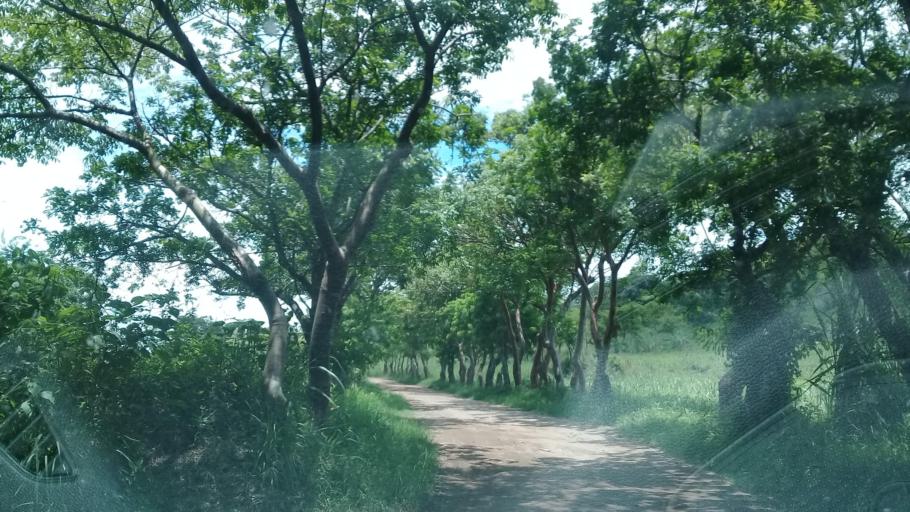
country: MX
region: Veracruz
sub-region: Naolinco
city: El Espinal
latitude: 19.5917
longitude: -96.8719
